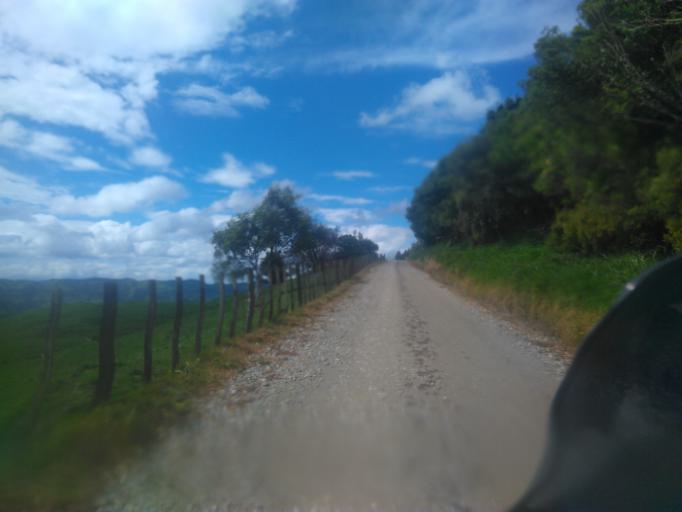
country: NZ
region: Hawke's Bay
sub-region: Wairoa District
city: Wairoa
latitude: -38.7760
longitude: 177.6339
